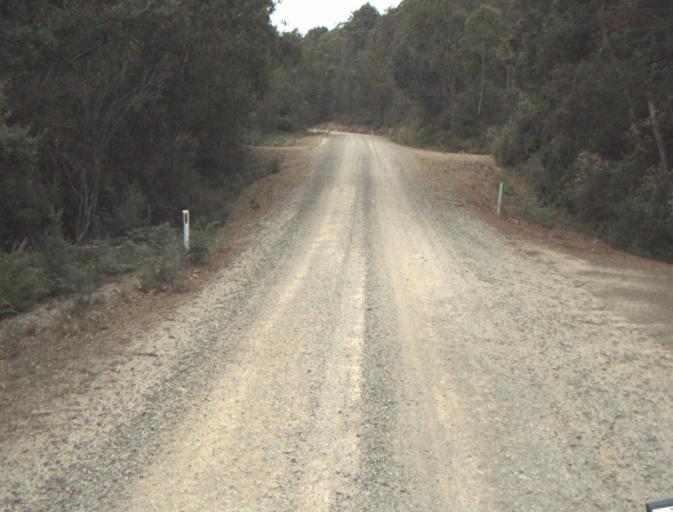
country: AU
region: Tasmania
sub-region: Dorset
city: Scottsdale
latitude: -41.3880
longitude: 147.5061
